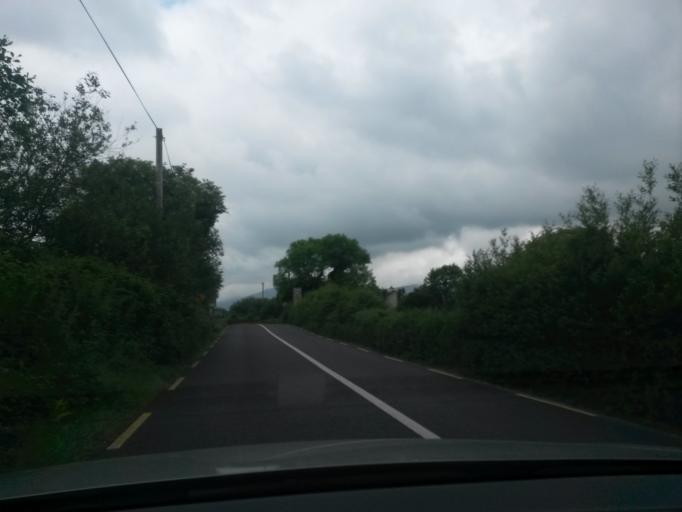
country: IE
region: Munster
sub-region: Ciarrai
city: Killorglin
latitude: 52.1637
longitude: -9.6975
